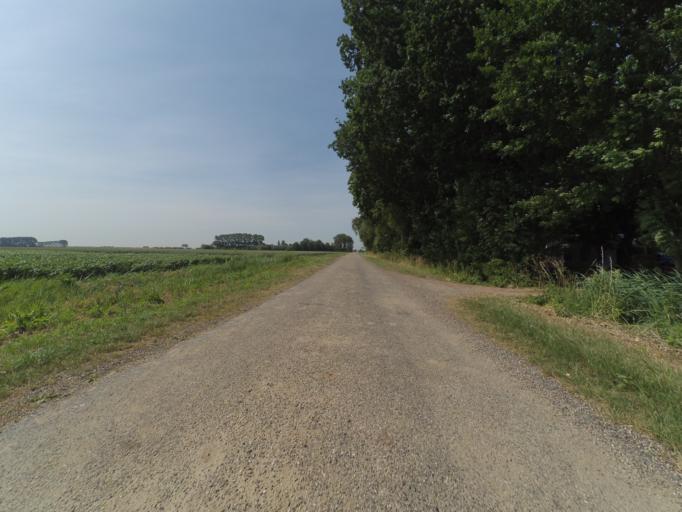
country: NL
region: Zeeland
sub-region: Schouwen-Duiveland
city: Bruinisse
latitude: 51.6476
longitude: 4.1381
